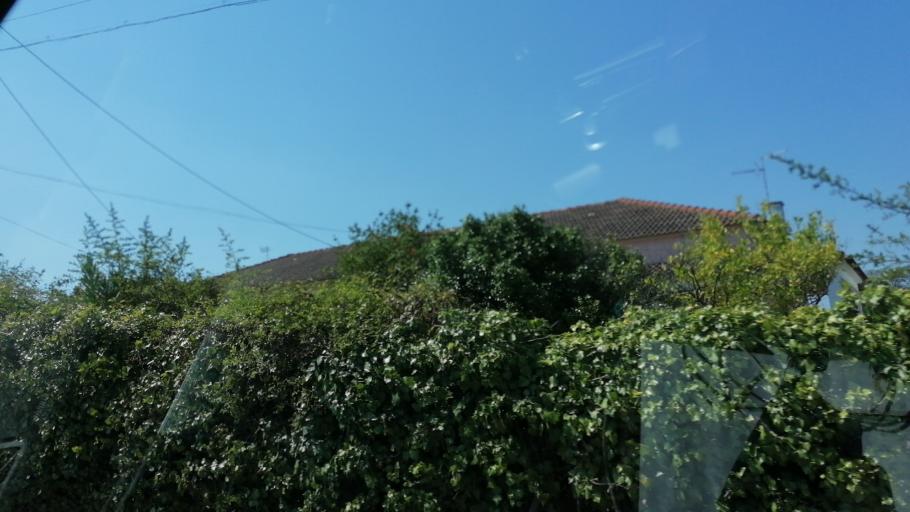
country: PT
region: Santarem
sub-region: Benavente
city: Poceirao
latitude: 38.7506
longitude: -8.6607
